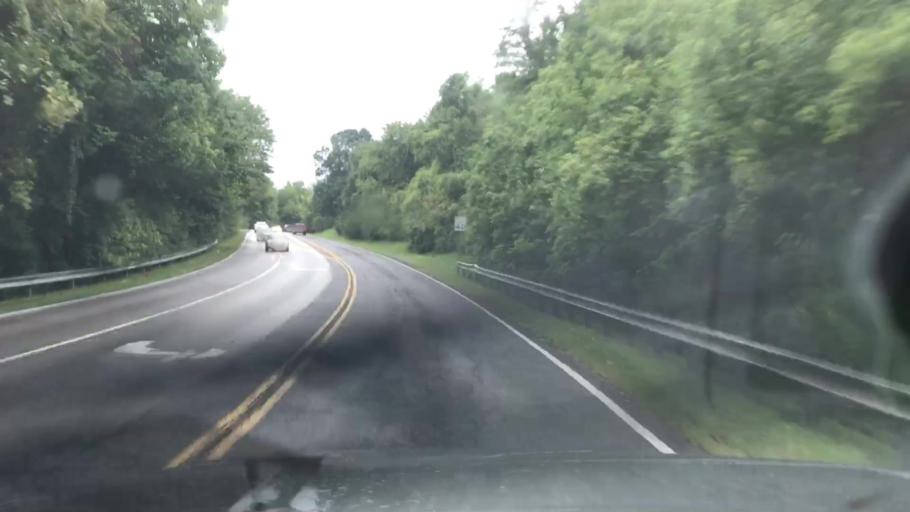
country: US
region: Tennessee
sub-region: Davidson County
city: Lakewood
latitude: 36.1630
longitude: -86.6133
